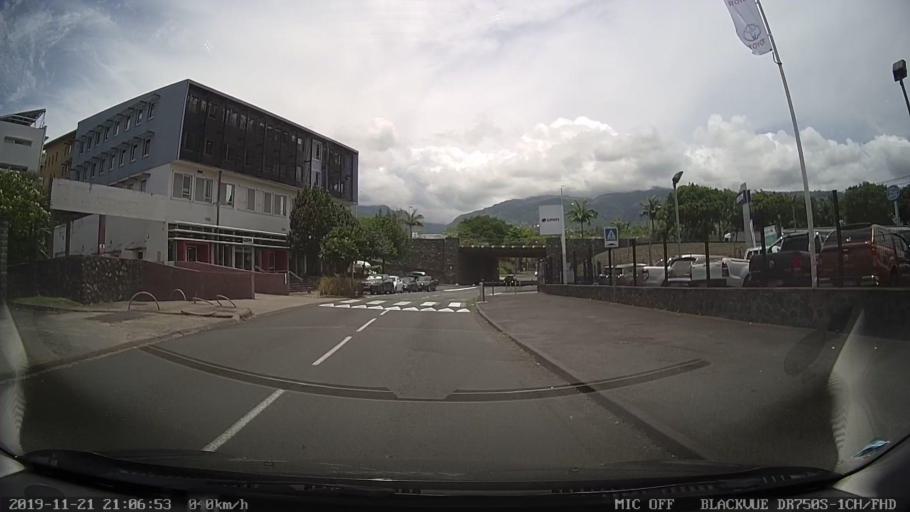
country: RE
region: Reunion
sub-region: Reunion
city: Sainte-Marie
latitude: -20.9016
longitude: 55.4994
